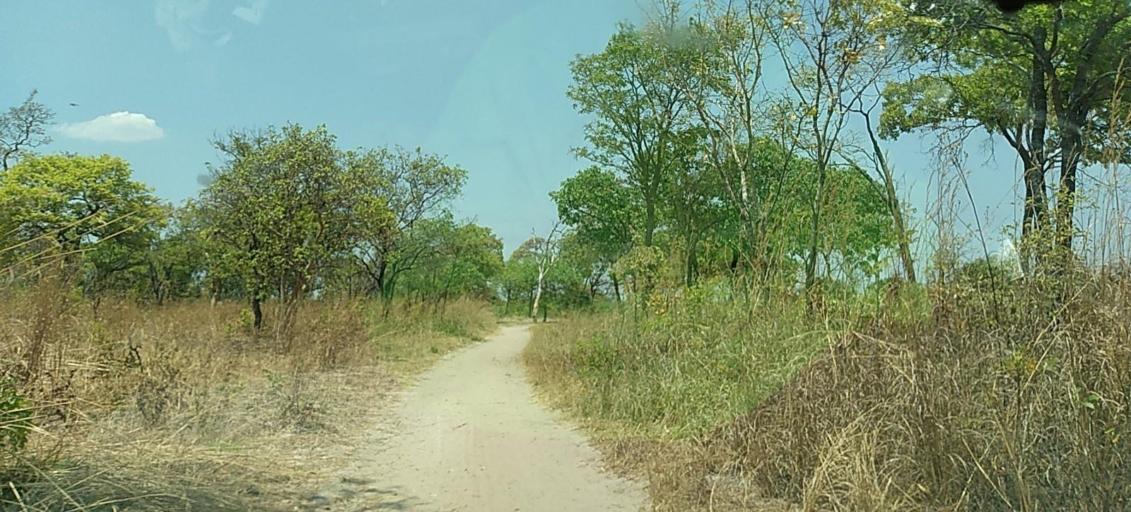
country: ZM
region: North-Western
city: Kabompo
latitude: -13.2728
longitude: 24.5518
